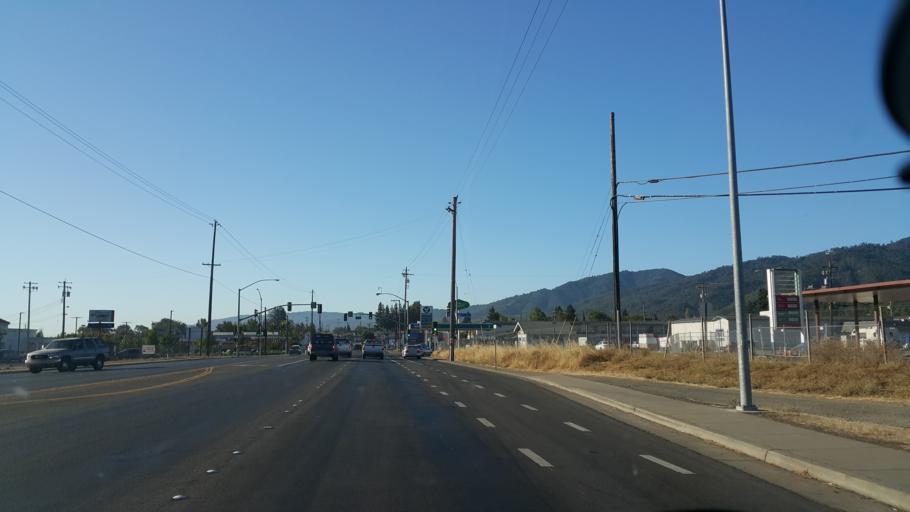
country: US
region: California
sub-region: Mendocino County
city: Ukiah
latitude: 39.1702
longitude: -123.2116
